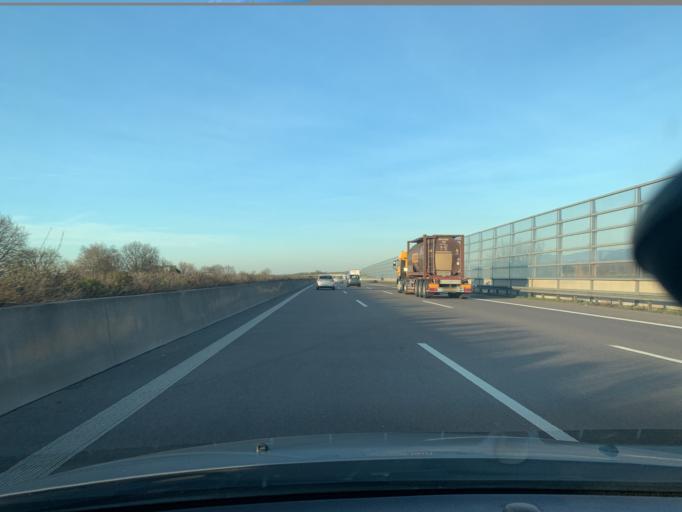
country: DE
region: Baden-Wuerttemberg
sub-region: Freiburg Region
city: Willstatt
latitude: 48.5162
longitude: 7.9146
